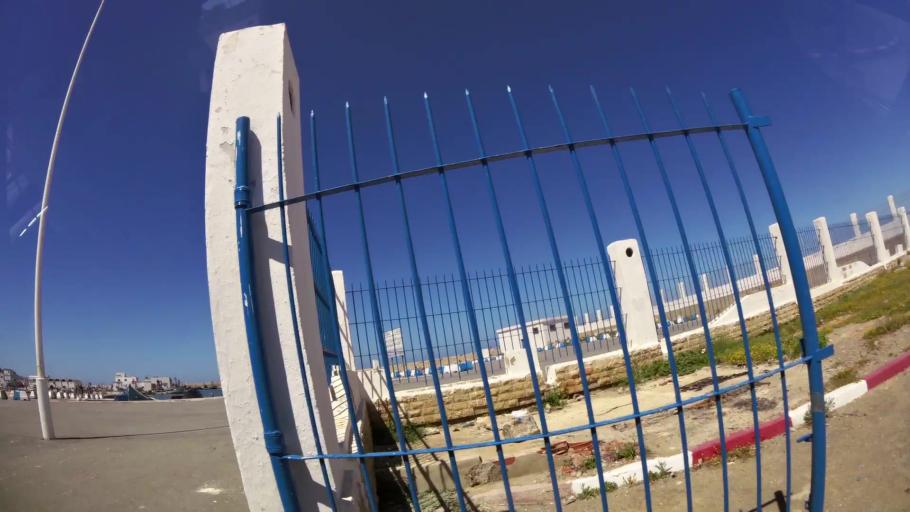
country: MA
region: Oriental
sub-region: Berkane-Taourirt
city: Madagh
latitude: 35.1435
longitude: -2.4218
